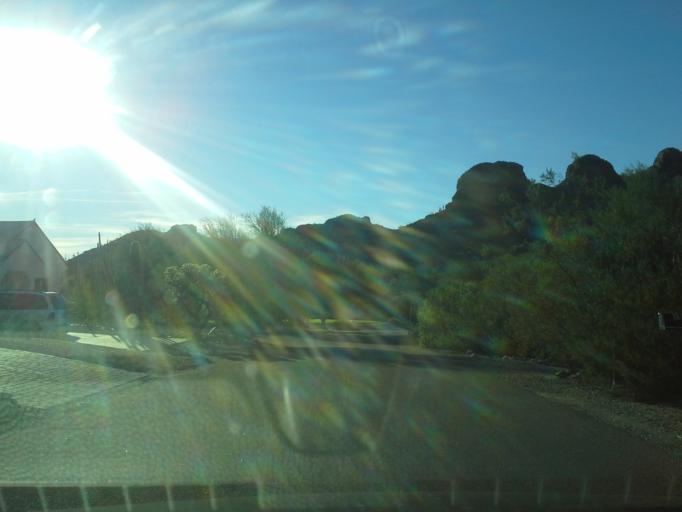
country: US
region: Arizona
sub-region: Pinal County
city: Apache Junction
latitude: 33.3652
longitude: -111.4373
